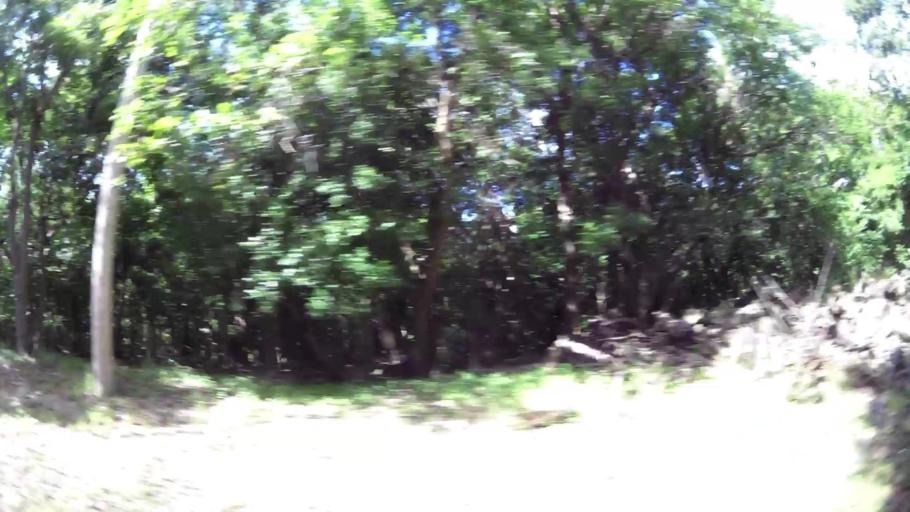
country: MS
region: Saint Peter
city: Saint Peters
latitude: 16.7517
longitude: -62.2229
